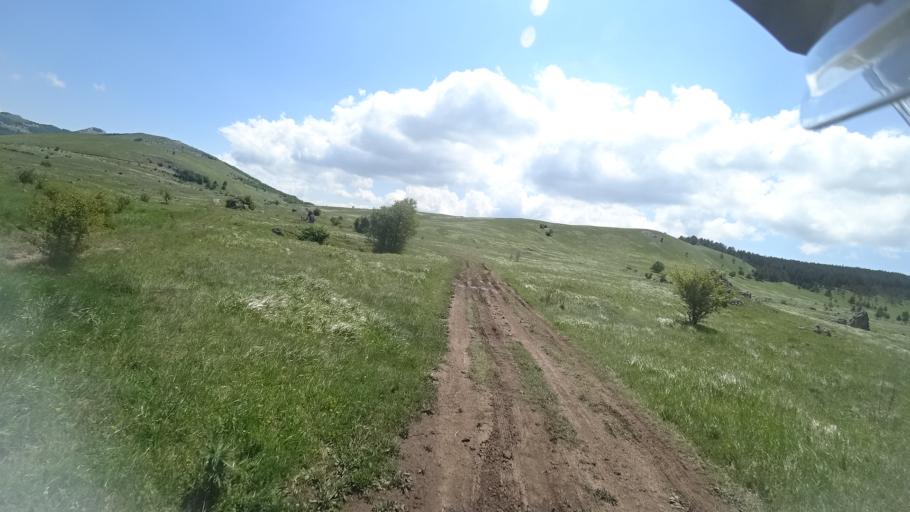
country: HR
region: Zadarska
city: Gracac
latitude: 44.3749
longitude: 15.9552
